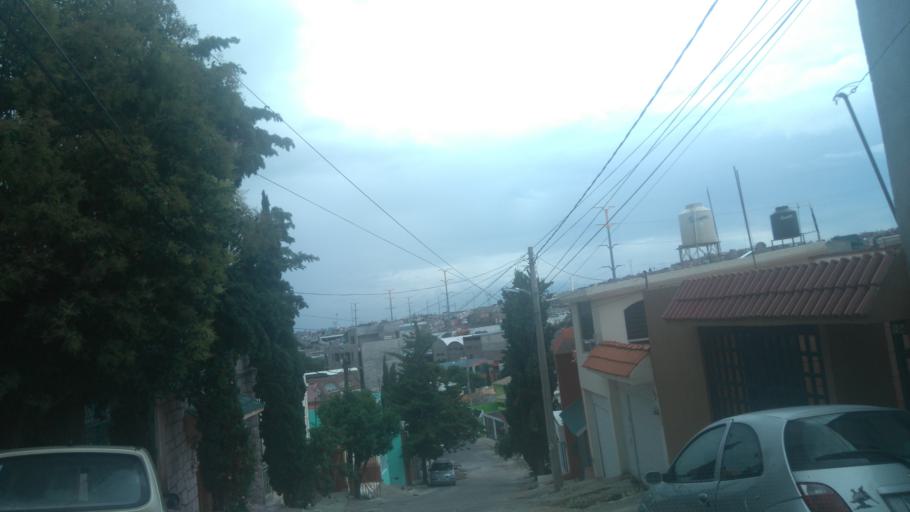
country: MX
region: Zacatecas
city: Zacatecas
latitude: 22.7564
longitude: -102.5877
